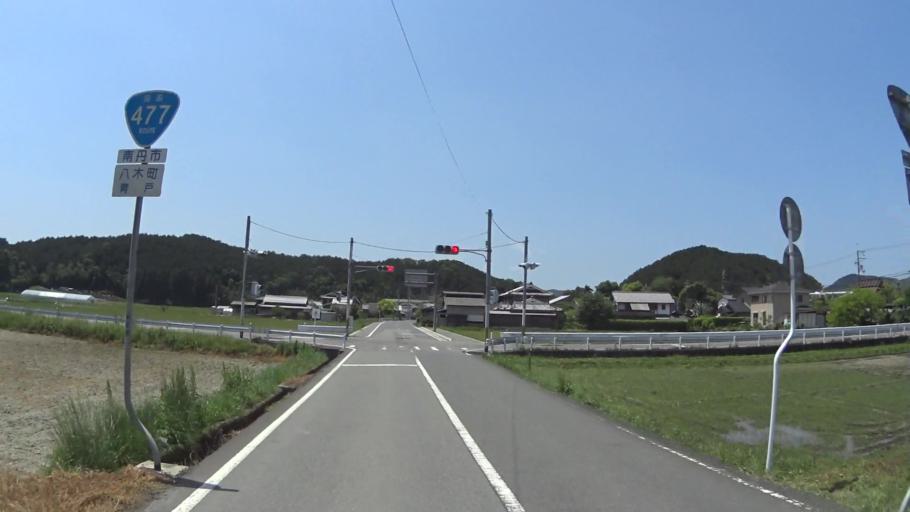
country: JP
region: Kyoto
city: Kameoka
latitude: 35.0772
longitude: 135.5504
